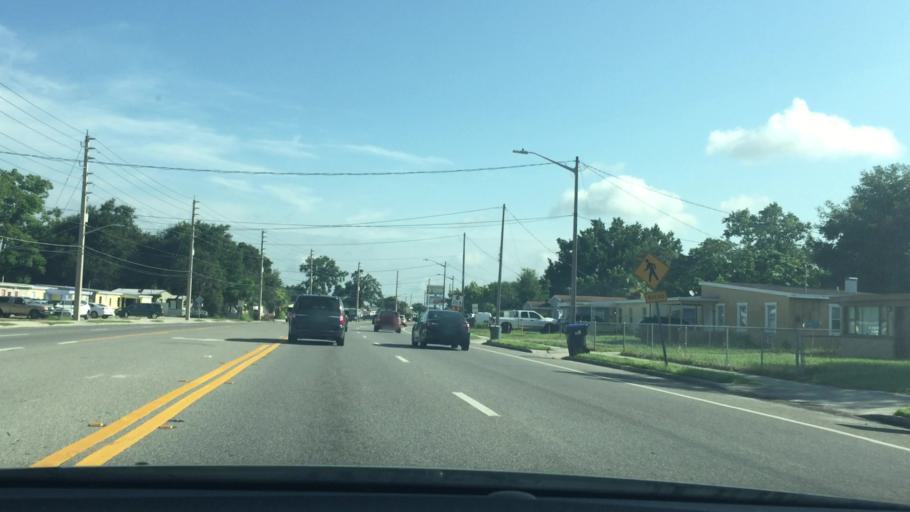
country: US
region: Florida
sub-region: Orange County
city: Pine Hills
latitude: 28.5736
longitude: -81.4518
